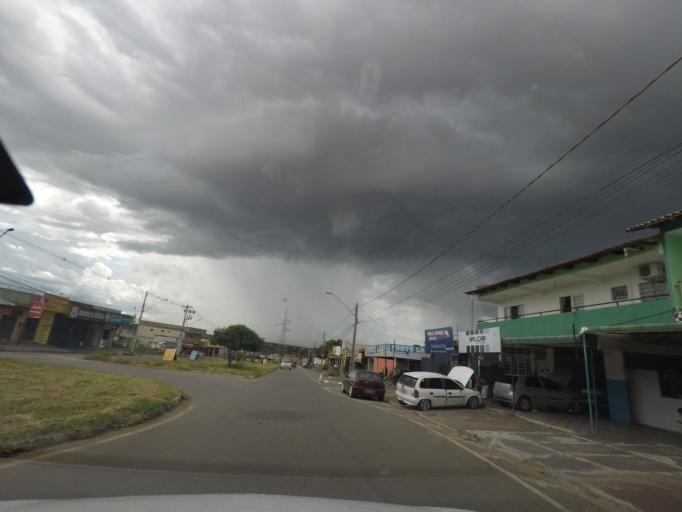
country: BR
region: Goias
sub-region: Goiania
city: Goiania
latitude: -16.7328
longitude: -49.3506
